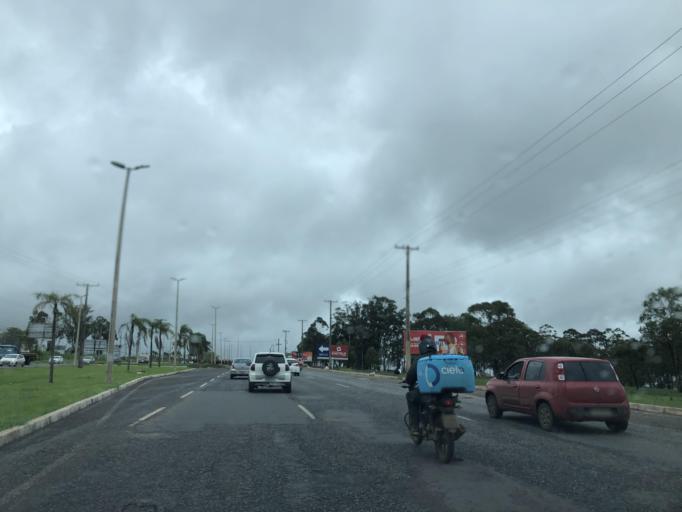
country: BR
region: Federal District
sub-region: Brasilia
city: Brasilia
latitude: -15.8410
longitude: -48.0753
